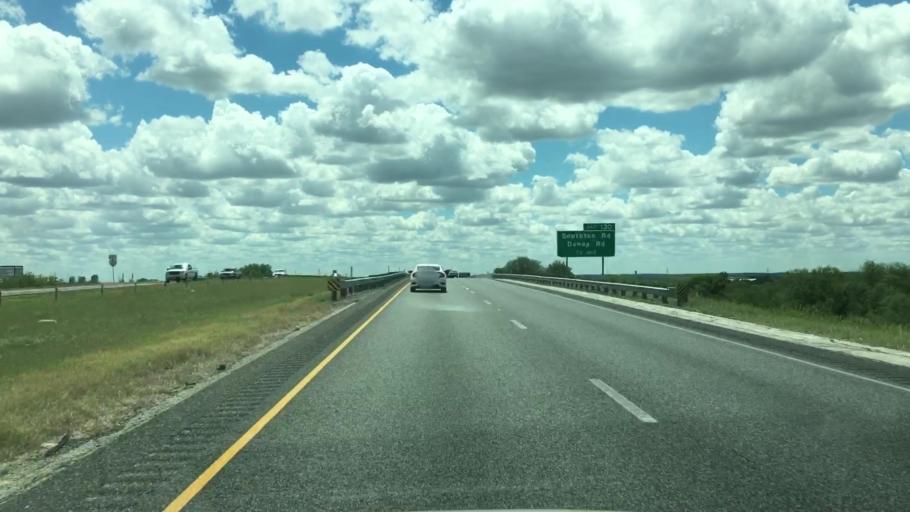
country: US
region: Texas
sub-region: Bexar County
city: Elmendorf
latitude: 29.2912
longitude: -98.3954
